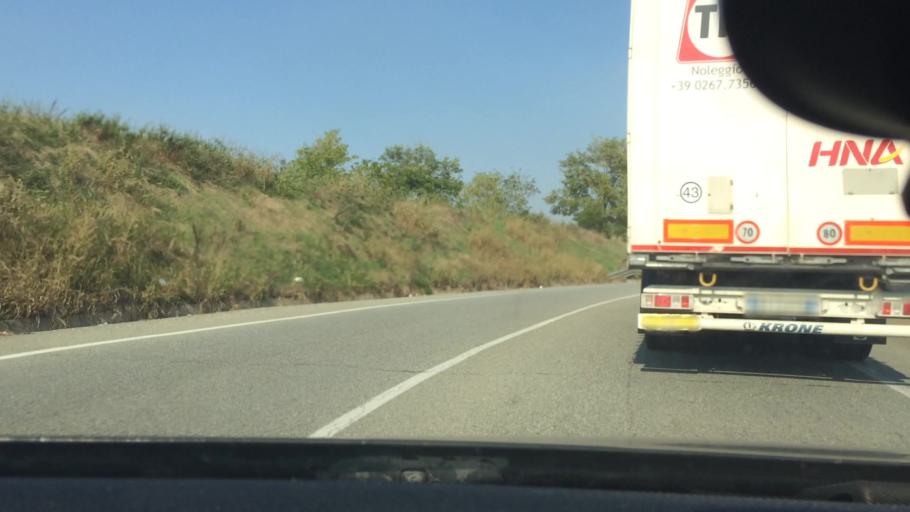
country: IT
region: Lombardy
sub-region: Citta metropolitana di Milano
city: Mantegazza
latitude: 45.5036
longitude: 8.9614
